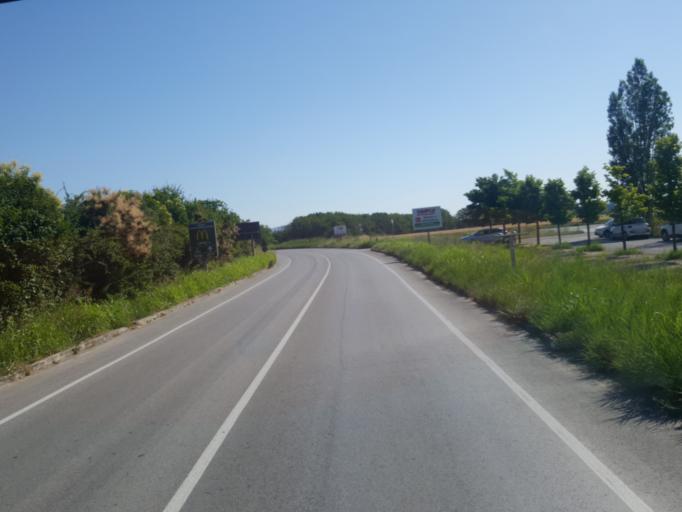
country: IT
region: The Marches
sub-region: Provincia di Pesaro e Urbino
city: Borgo Santa Maria
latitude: 43.8726
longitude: 12.8050
